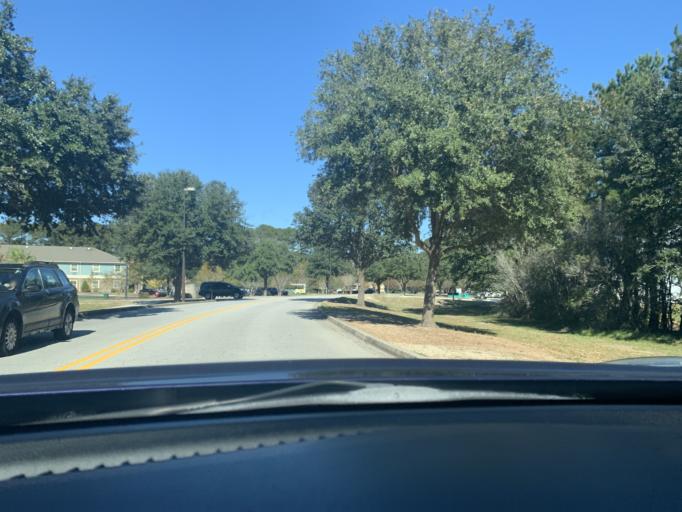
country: US
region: Georgia
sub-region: Chatham County
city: Pooler
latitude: 32.1334
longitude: -81.2583
